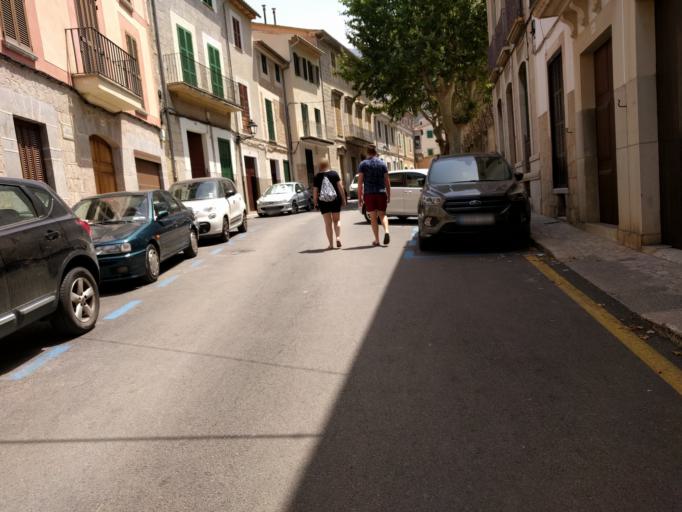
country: ES
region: Balearic Islands
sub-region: Illes Balears
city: Soller
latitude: 39.7685
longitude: 2.7155
